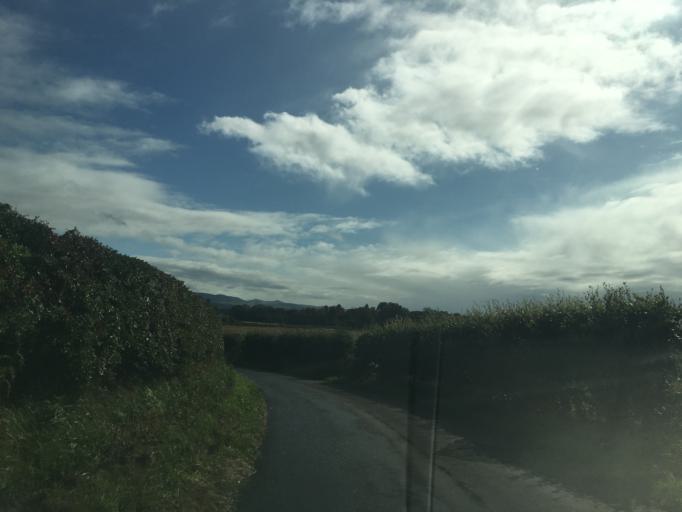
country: GB
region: Scotland
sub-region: Edinburgh
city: Kirkliston
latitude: 55.9621
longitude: -3.3758
